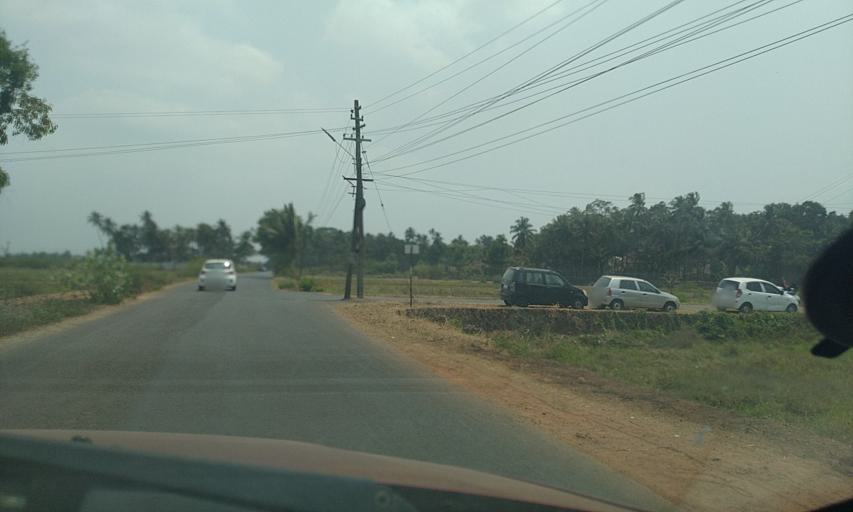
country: IN
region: Goa
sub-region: North Goa
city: Saligao
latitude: 15.5517
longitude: 73.7837
